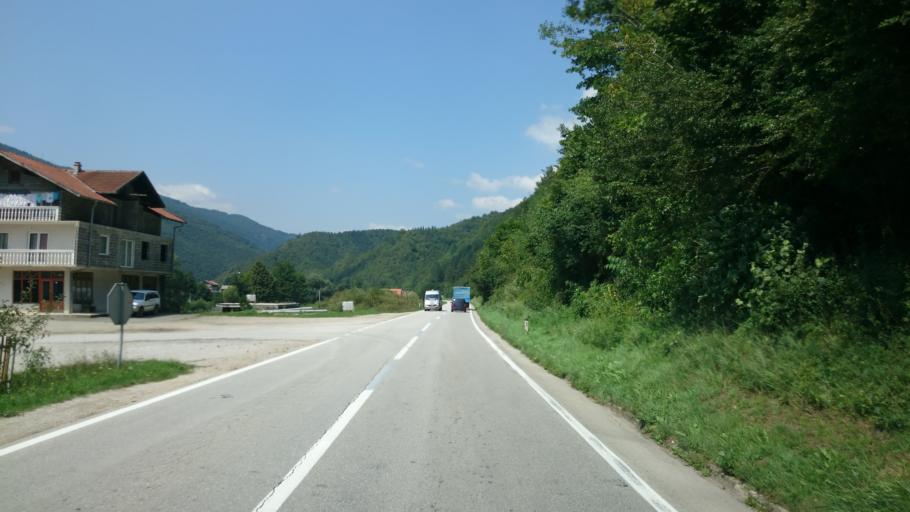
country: BA
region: Federation of Bosnia and Herzegovina
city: Donji Vakuf
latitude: 44.1777
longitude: 17.3552
